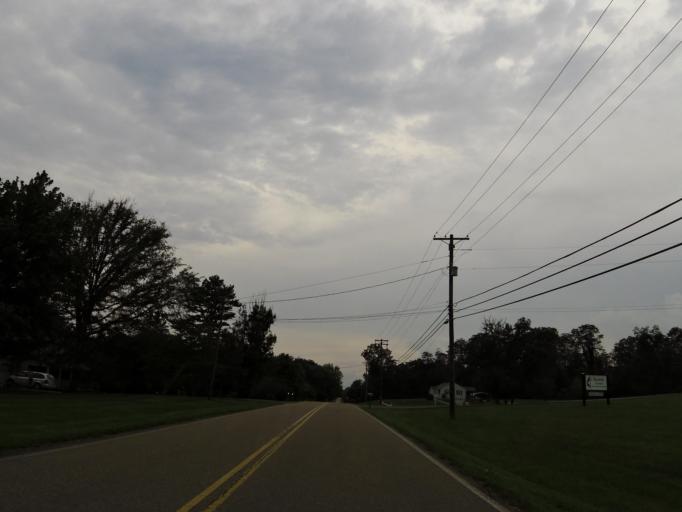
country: US
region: Tennessee
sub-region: Sevier County
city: Seymour
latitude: 35.9271
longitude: -83.8046
